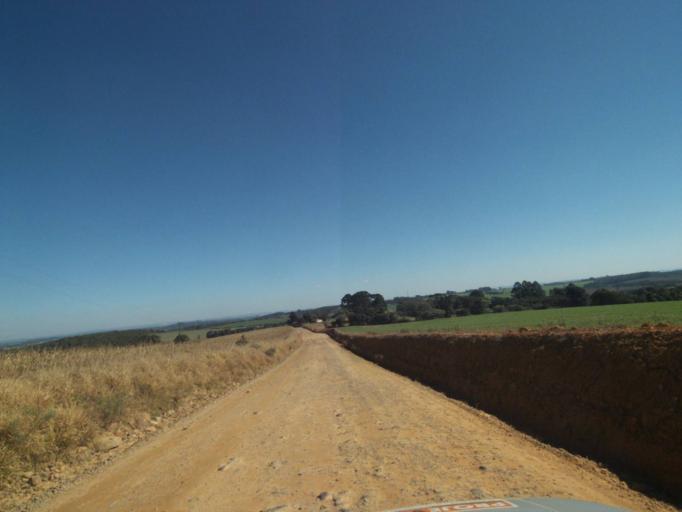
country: BR
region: Parana
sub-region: Tibagi
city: Tibagi
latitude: -24.6195
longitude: -50.6107
